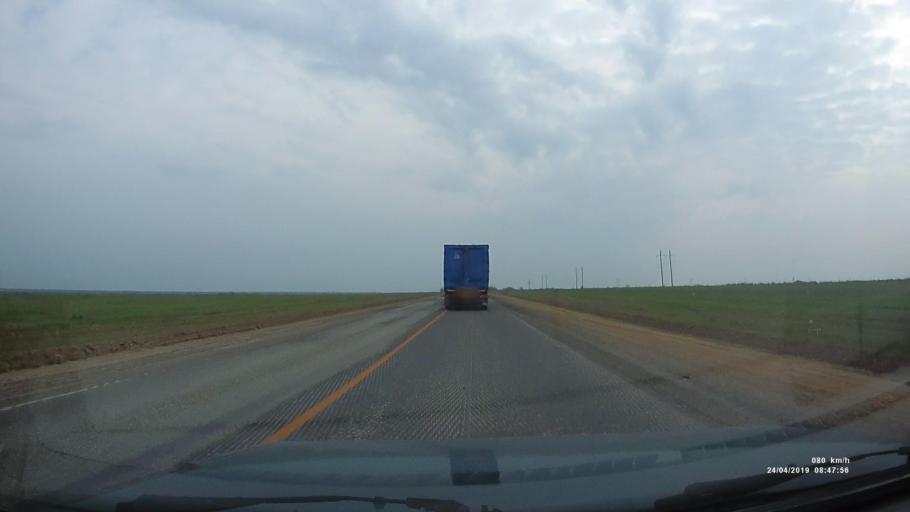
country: RU
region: Kalmykiya
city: Arshan'
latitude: 46.2481
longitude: 44.1015
